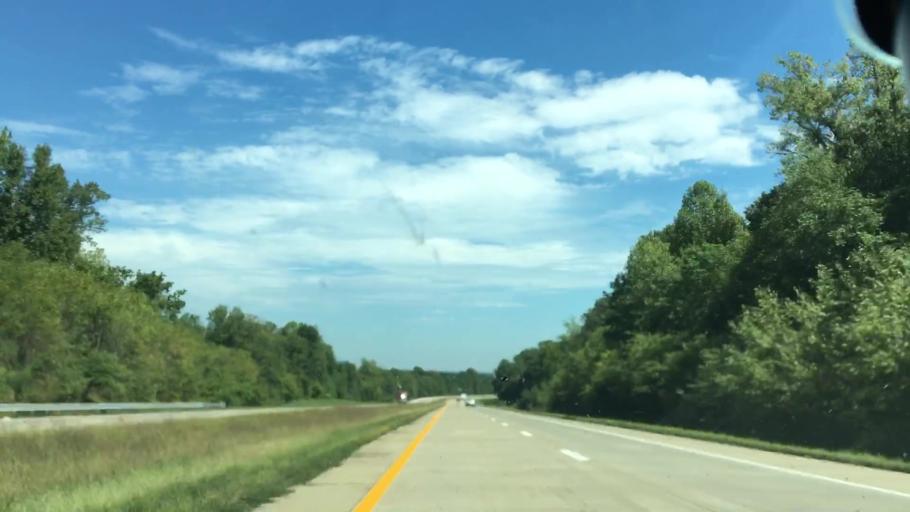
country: US
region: Indiana
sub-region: Warrick County
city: Newburgh
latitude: 37.7612
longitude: -87.3227
